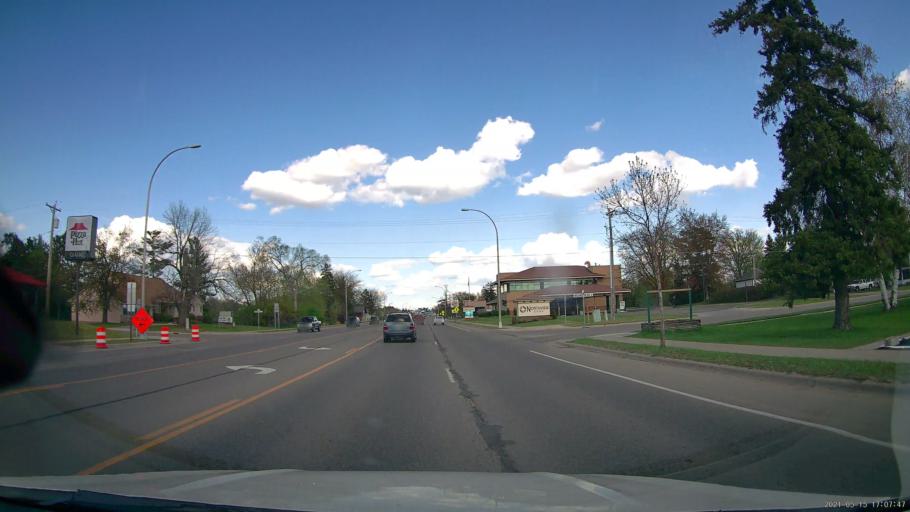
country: US
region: Minnesota
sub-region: Hubbard County
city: Park Rapids
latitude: 46.9221
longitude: -95.0575
